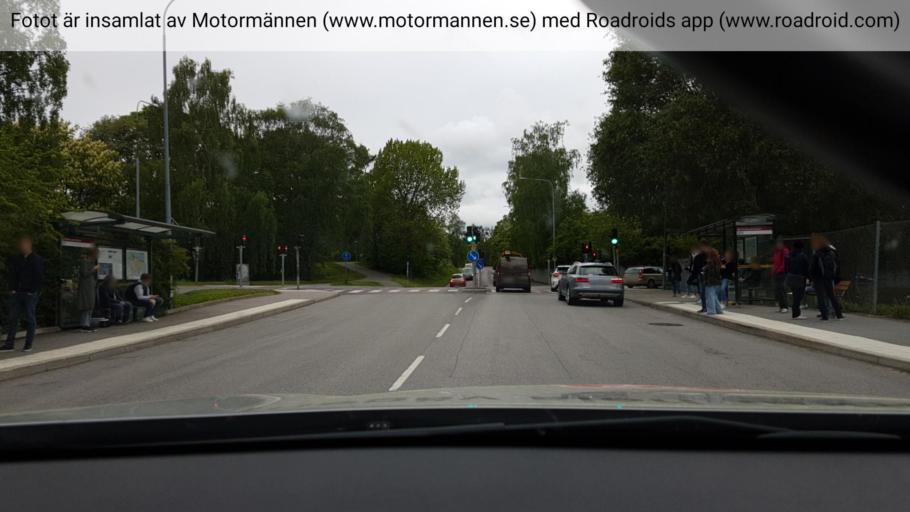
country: SE
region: Stockholm
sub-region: Lidingo
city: Lidingoe
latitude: 59.3625
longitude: 18.1523
